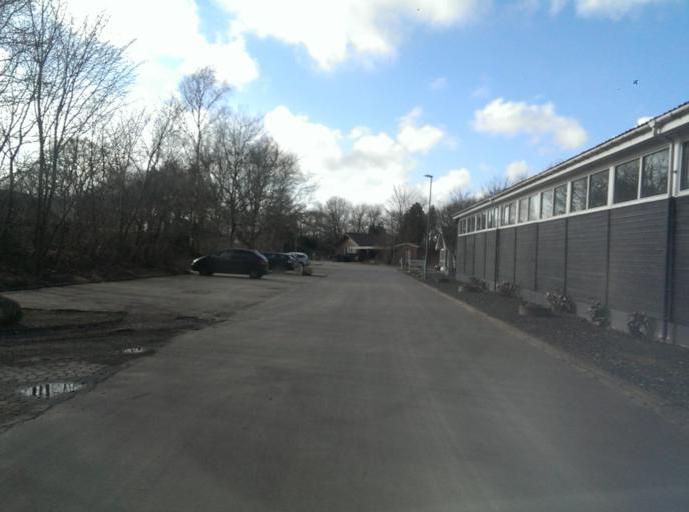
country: DK
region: South Denmark
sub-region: Esbjerg Kommune
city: Bramming
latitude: 55.4633
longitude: 8.7112
